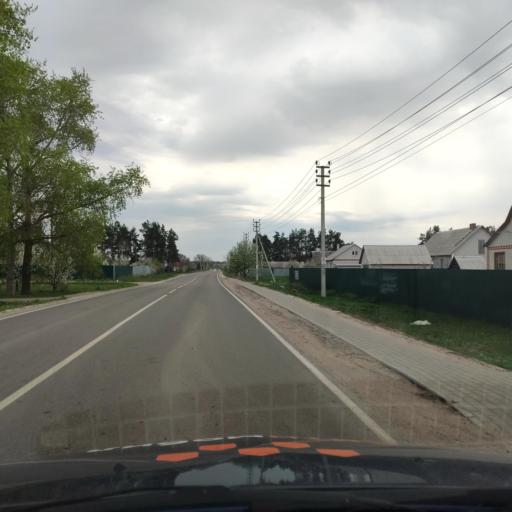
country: RU
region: Voronezj
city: Podgornoye
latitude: 51.8776
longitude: 39.1731
